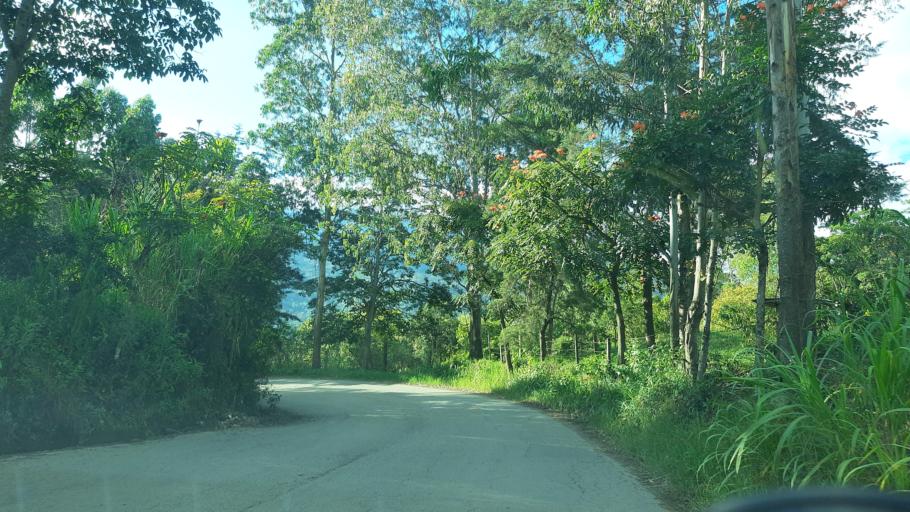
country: CO
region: Boyaca
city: Garagoa
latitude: 5.0755
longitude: -73.3783
